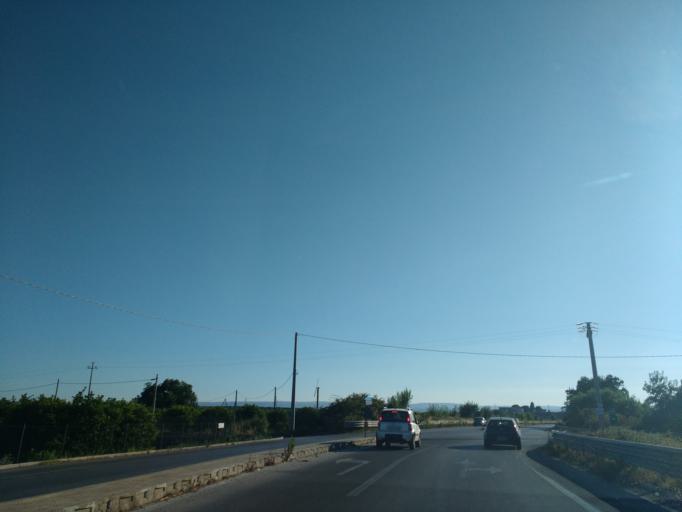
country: IT
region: Sicily
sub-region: Provincia di Siracusa
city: Belvedere
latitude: 37.0617
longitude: 15.2379
